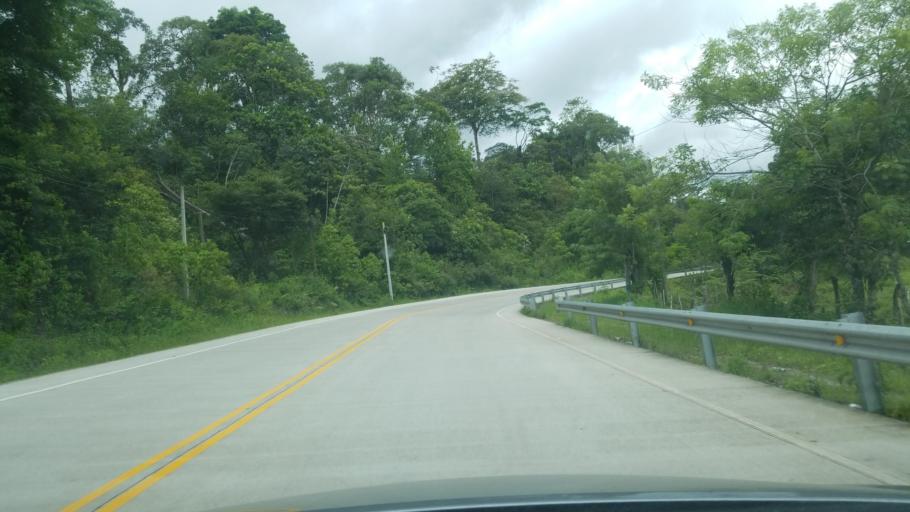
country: HN
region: Copan
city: San Jeronimo
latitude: 14.9494
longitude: -88.9086
